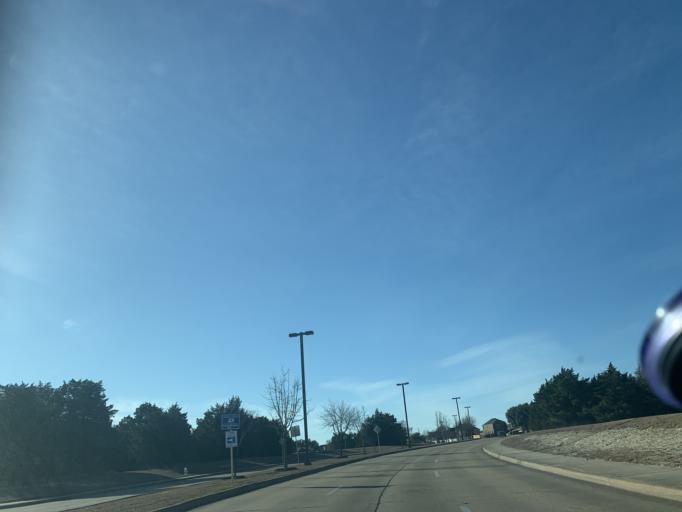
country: US
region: Texas
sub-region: Dallas County
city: DeSoto
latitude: 32.5888
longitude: -96.8389
